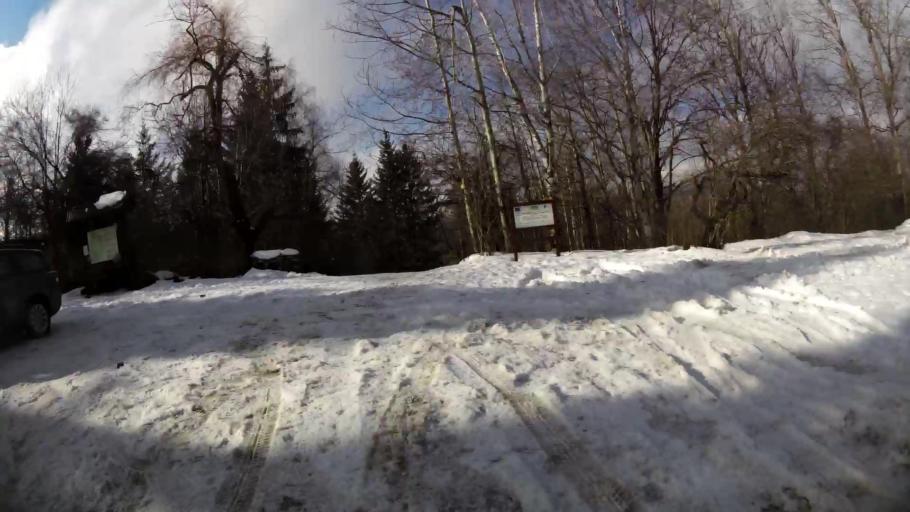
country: BG
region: Sofia-Capital
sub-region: Stolichna Obshtina
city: Sofia
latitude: 42.6284
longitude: 23.2301
